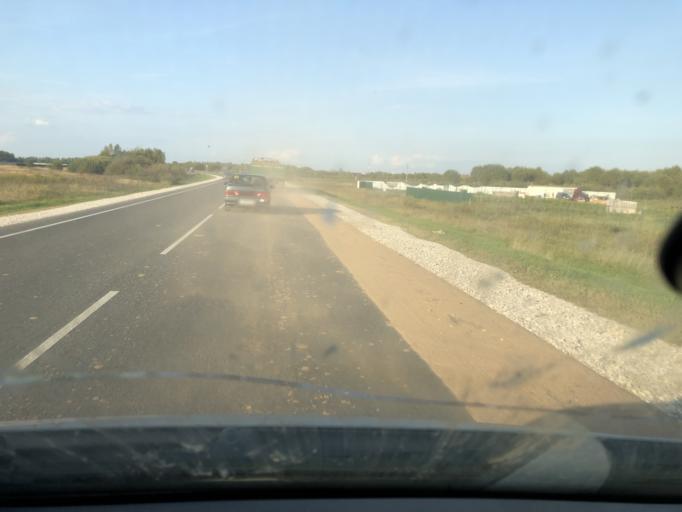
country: RU
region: Kaluga
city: Peremyshl'
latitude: 54.2616
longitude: 36.1311
